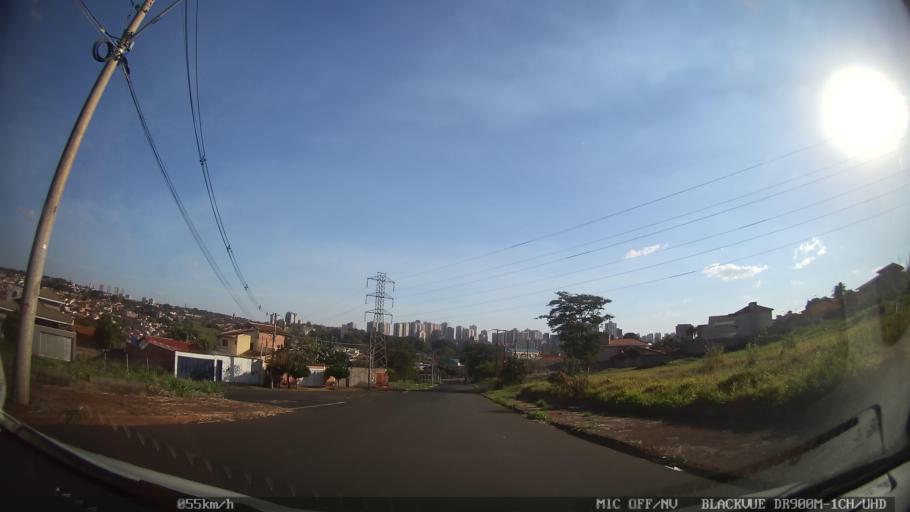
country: BR
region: Sao Paulo
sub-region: Ribeirao Preto
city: Ribeirao Preto
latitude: -21.2072
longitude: -47.7828
